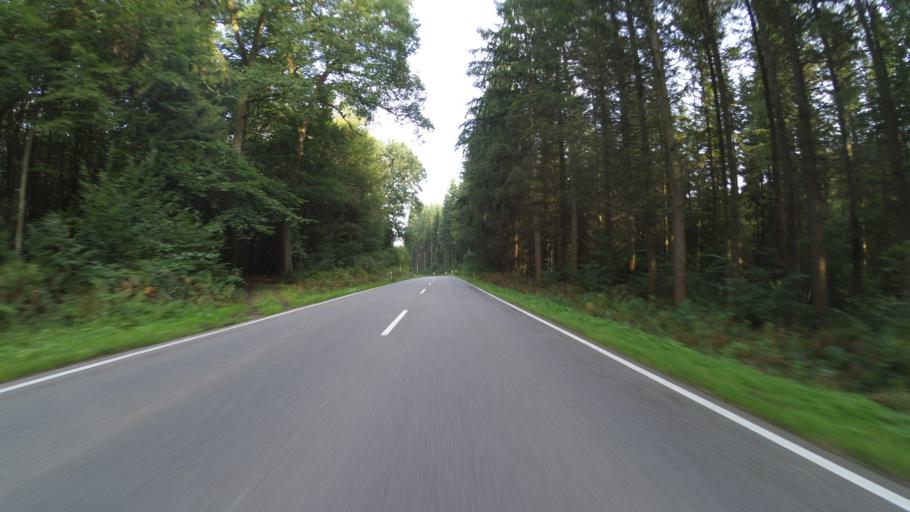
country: DE
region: Saarland
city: Wadern
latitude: 49.5402
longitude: 6.8571
